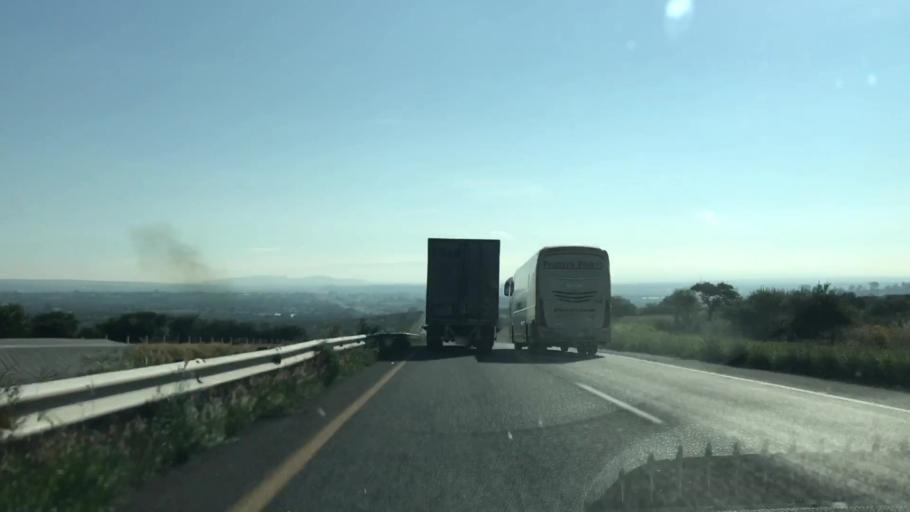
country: MX
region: Jalisco
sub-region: Lagos de Moreno
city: Cristeros [Fraccionamiento]
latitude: 21.3081
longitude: -102.0723
